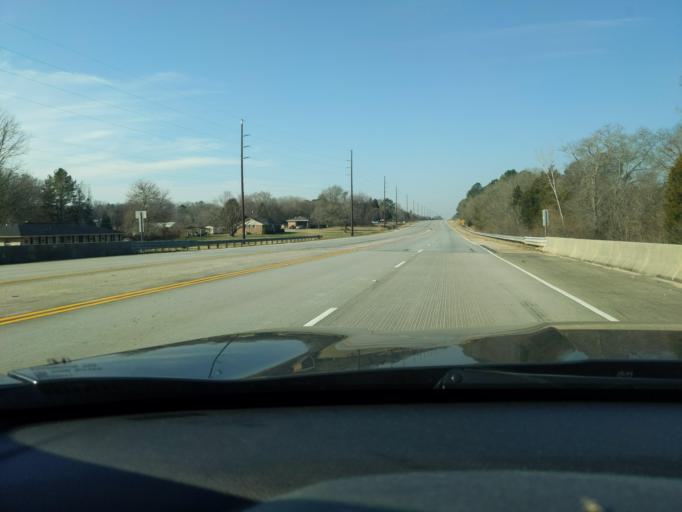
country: US
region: South Carolina
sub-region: Abbeville County
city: Calhoun Falls
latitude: 34.1058
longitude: -82.5308
